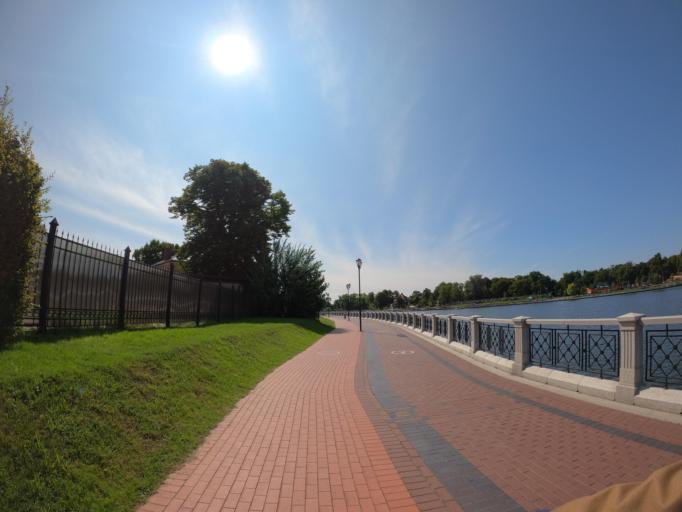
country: RU
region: Kaliningrad
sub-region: Gorod Kaliningrad
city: Kaliningrad
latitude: 54.7266
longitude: 20.5195
